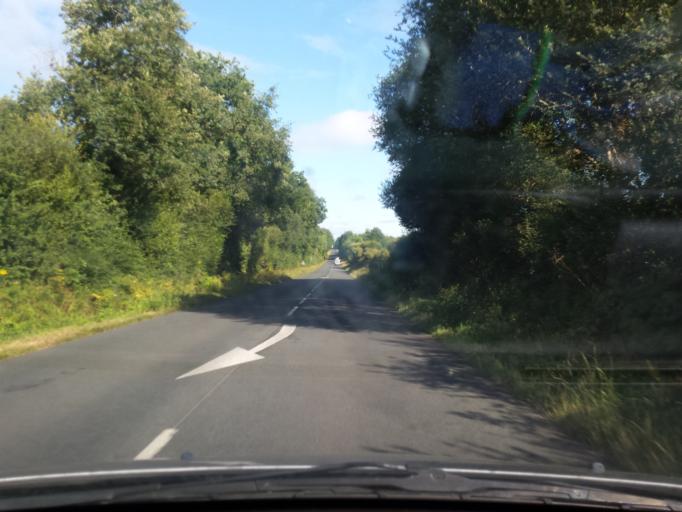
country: FR
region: Pays de la Loire
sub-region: Departement de la Vendee
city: La Mothe-Achard
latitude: 46.6266
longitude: -1.6844
